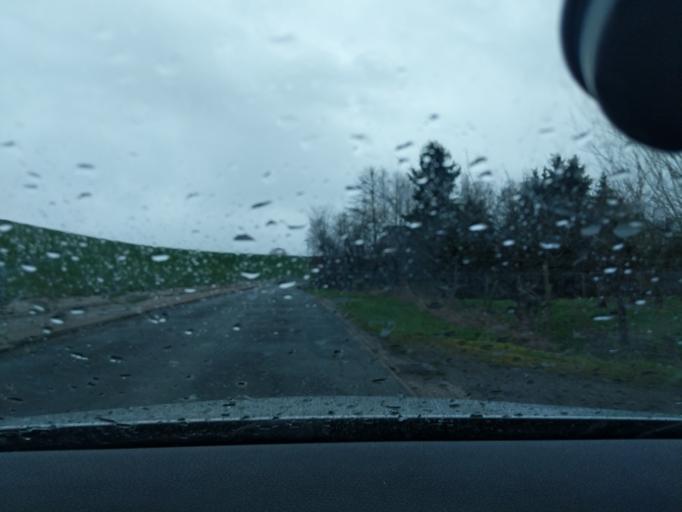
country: DE
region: Schleswig-Holstein
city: Haseldorf
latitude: 53.5884
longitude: 9.5843
